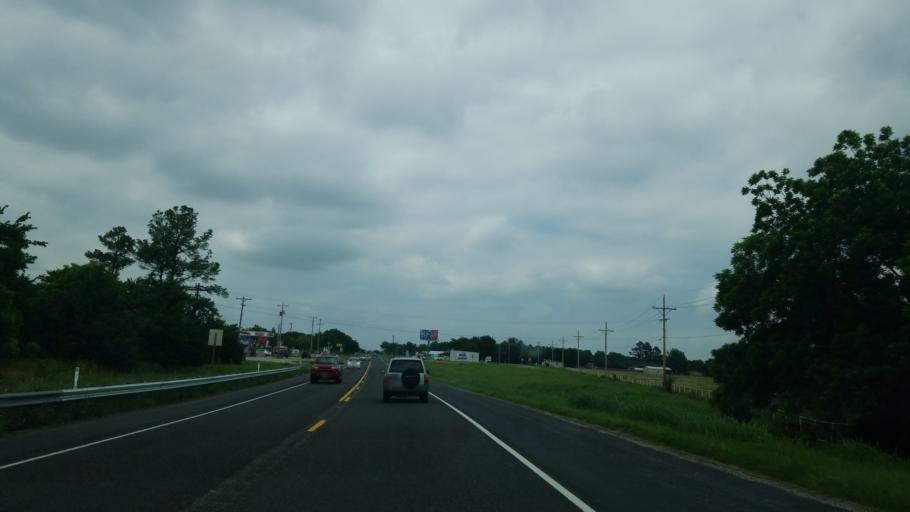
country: US
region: Texas
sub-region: Denton County
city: Pilot Point
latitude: 33.4591
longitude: -96.9197
